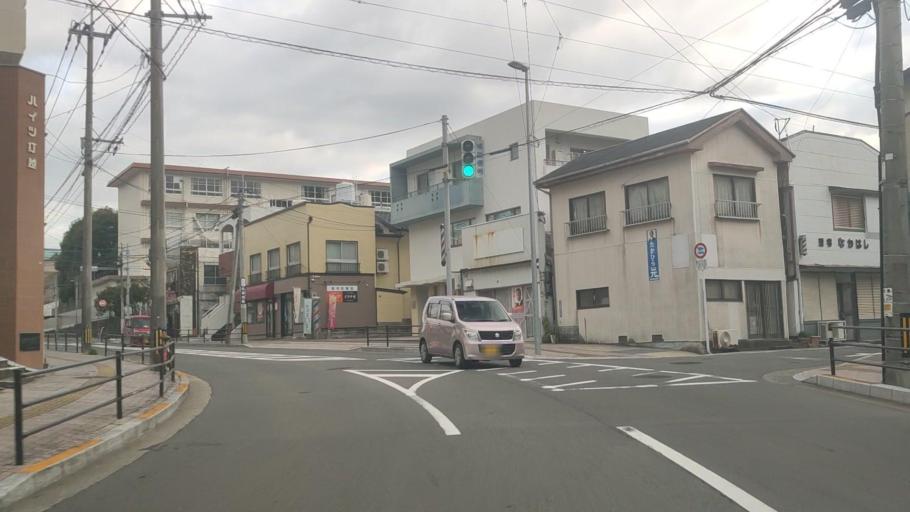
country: JP
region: Nagasaki
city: Nagasaki-shi
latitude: 32.7777
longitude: 129.8692
